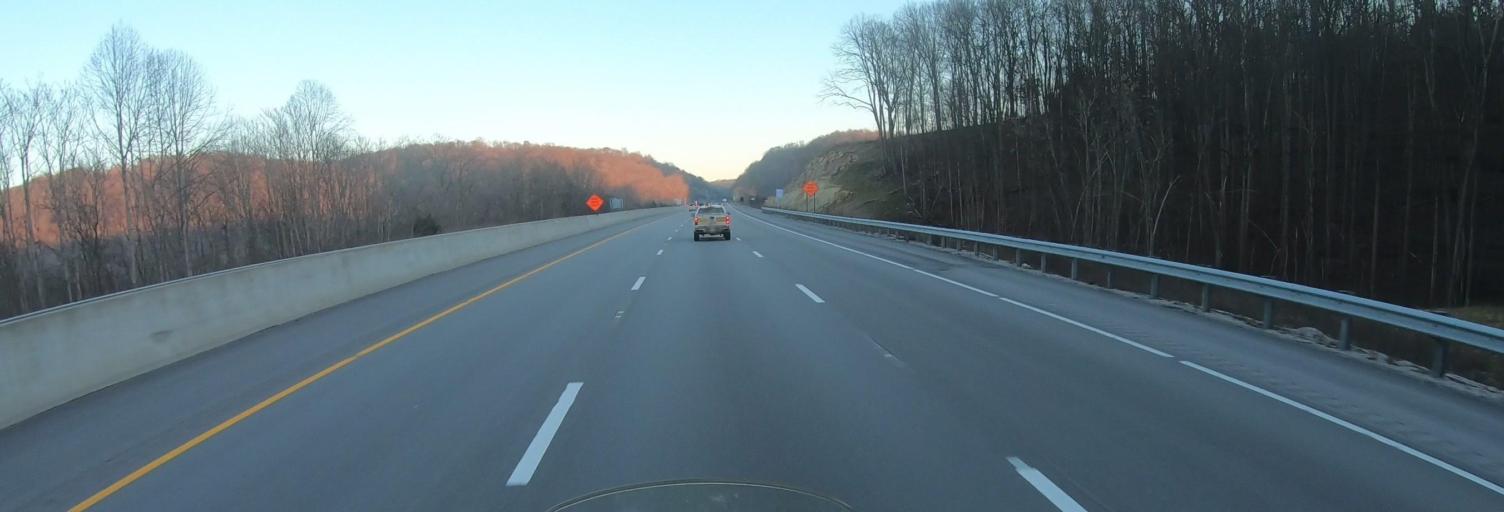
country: US
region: Kentucky
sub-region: Rockcastle County
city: Mount Vernon
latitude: 37.3734
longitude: -84.3237
